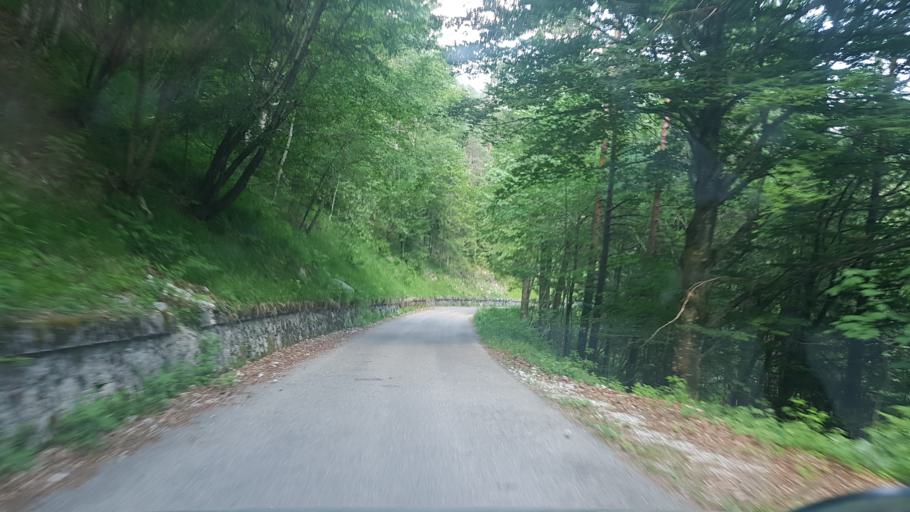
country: IT
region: Friuli Venezia Giulia
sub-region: Provincia di Udine
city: Pontebba
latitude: 46.5264
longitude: 13.2225
